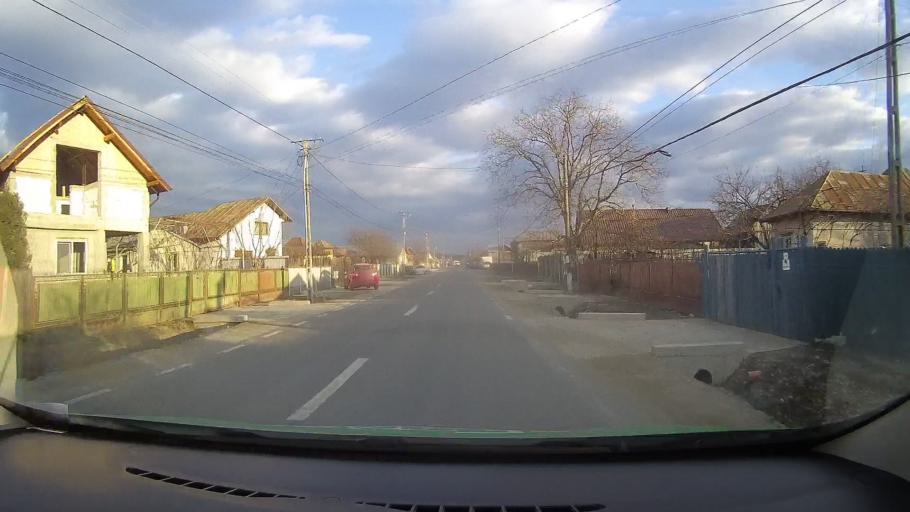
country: RO
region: Dambovita
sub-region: Comuna I. L. Caragiale
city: Ghirdoveni
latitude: 44.9442
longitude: 25.6653
